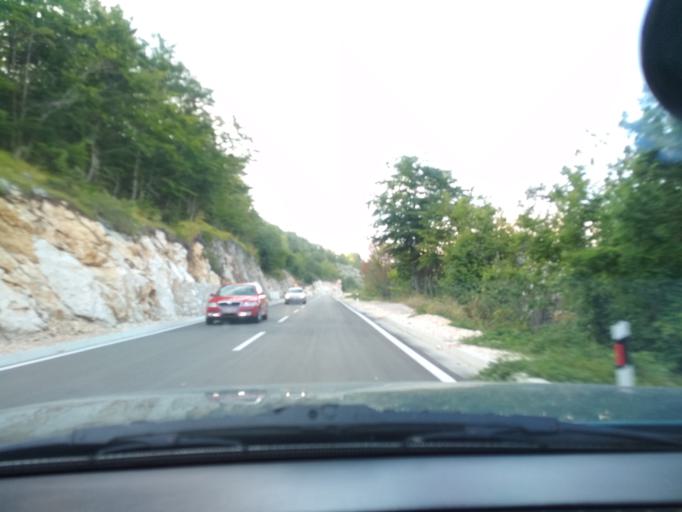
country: ME
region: Cetinje
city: Cetinje
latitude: 42.4313
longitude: 18.8585
